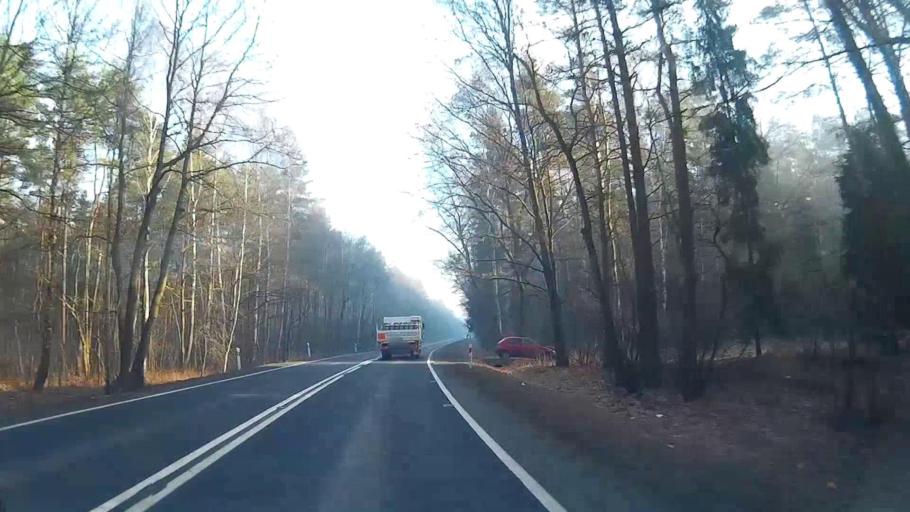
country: PL
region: Lesser Poland Voivodeship
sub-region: Powiat oswiecimski
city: Chelmek
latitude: 50.0768
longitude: 19.2668
